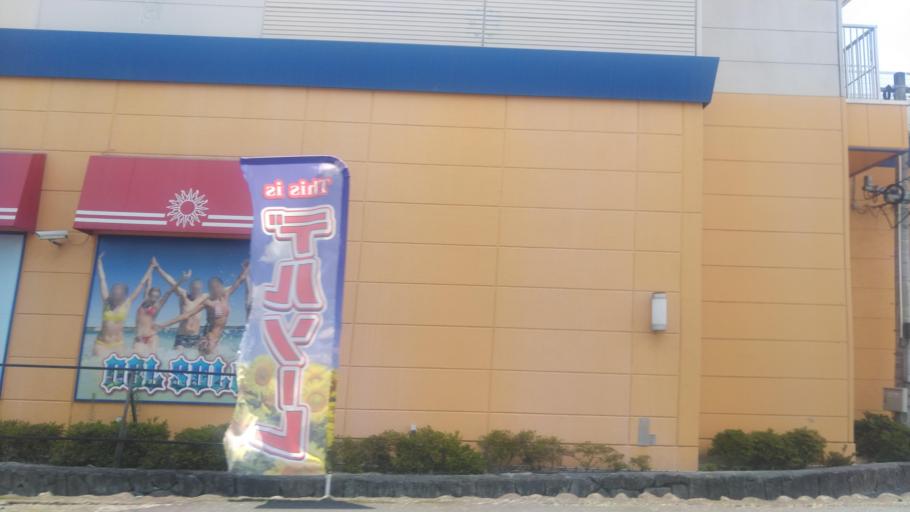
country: JP
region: Oita
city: Hita
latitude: 33.3223
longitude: 130.9261
